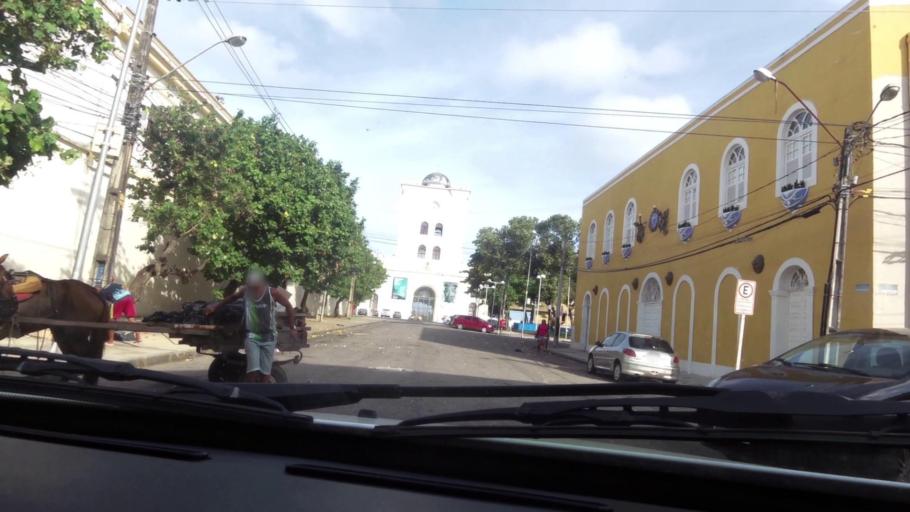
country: BR
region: Pernambuco
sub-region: Recife
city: Recife
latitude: -8.0605
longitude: -34.8718
